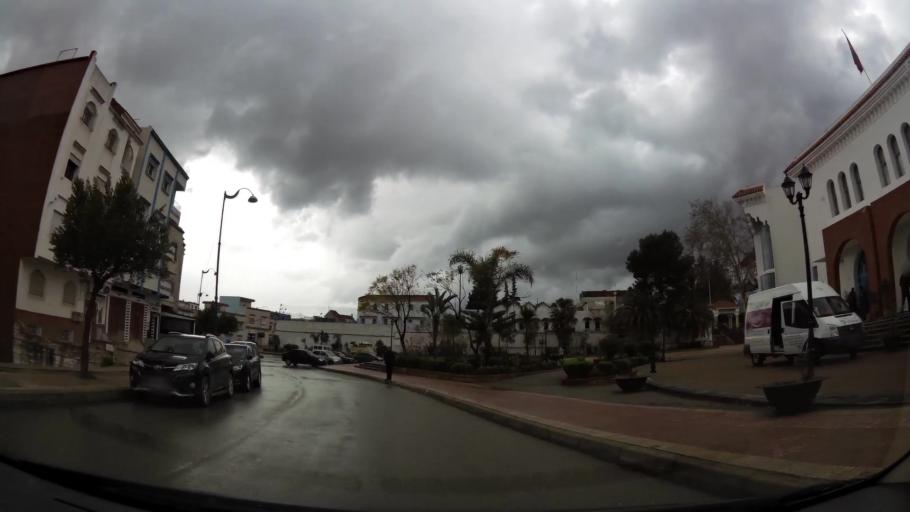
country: MA
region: Tanger-Tetouan
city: Chefchaouene
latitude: 35.1691
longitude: -5.2721
